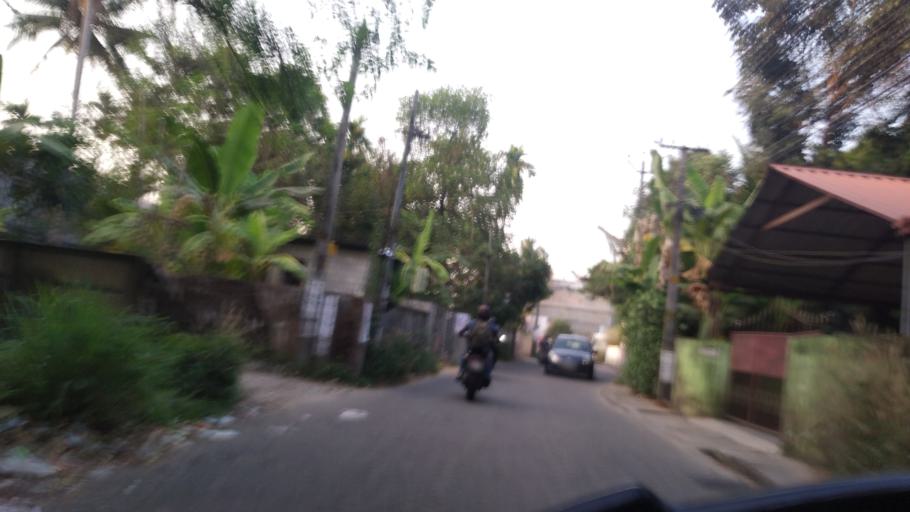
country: IN
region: Kerala
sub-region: Ernakulam
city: Elur
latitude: 10.0339
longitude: 76.2761
